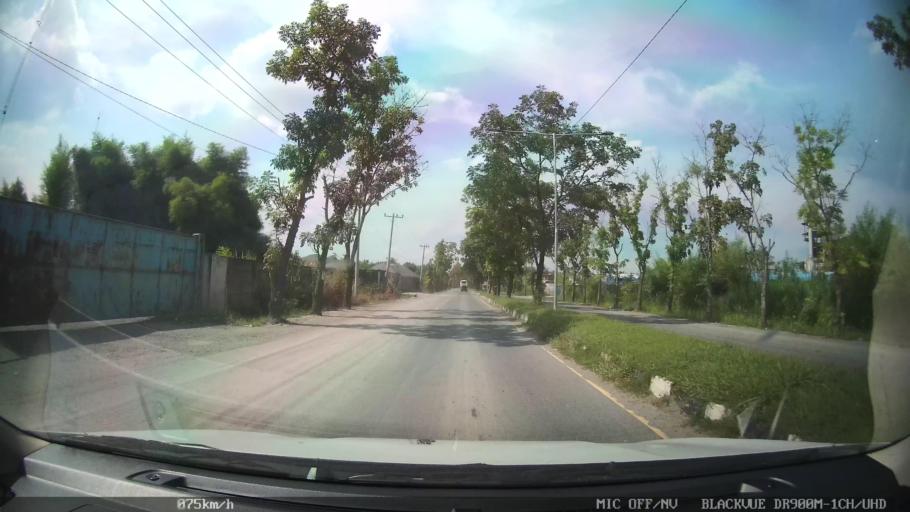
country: ID
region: North Sumatra
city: Binjai
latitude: 3.6324
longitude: 98.5351
